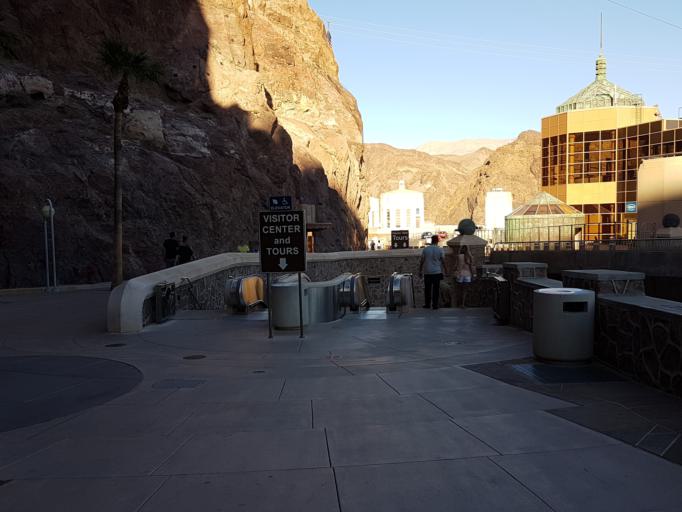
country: US
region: Nevada
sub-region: Clark County
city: Boulder City
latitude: 36.0161
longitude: -114.7397
